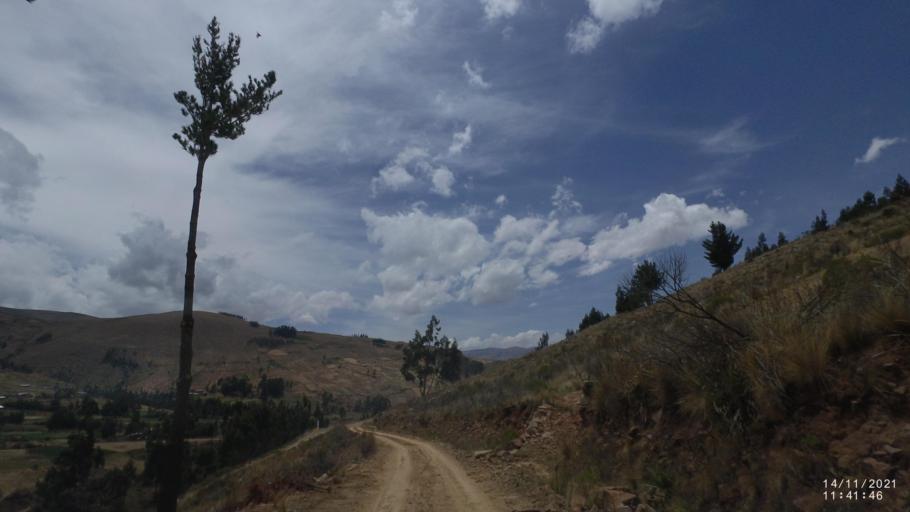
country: BO
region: Cochabamba
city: Colomi
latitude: -17.3539
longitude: -65.9916
